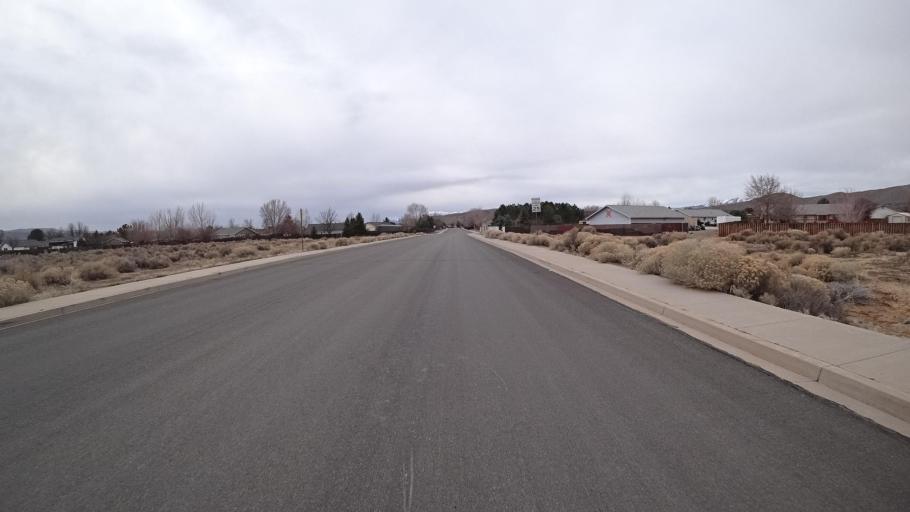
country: US
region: Nevada
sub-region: Washoe County
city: Spanish Springs
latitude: 39.6401
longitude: -119.7169
